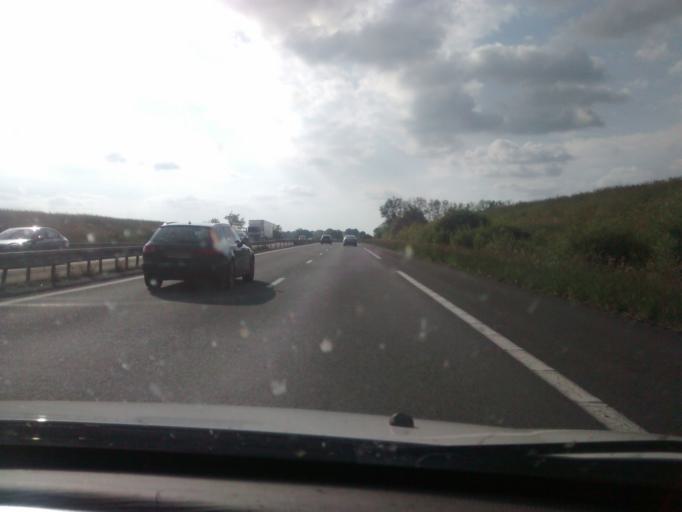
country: FR
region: Pays de la Loire
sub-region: Departement de la Mayenne
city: Argentre
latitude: 48.0807
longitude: -0.6586
